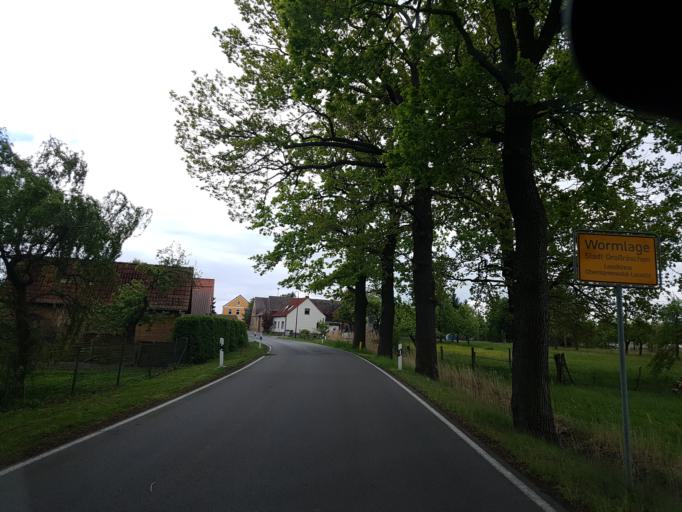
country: DE
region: Brandenburg
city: Sallgast
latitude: 51.6065
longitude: 13.9021
